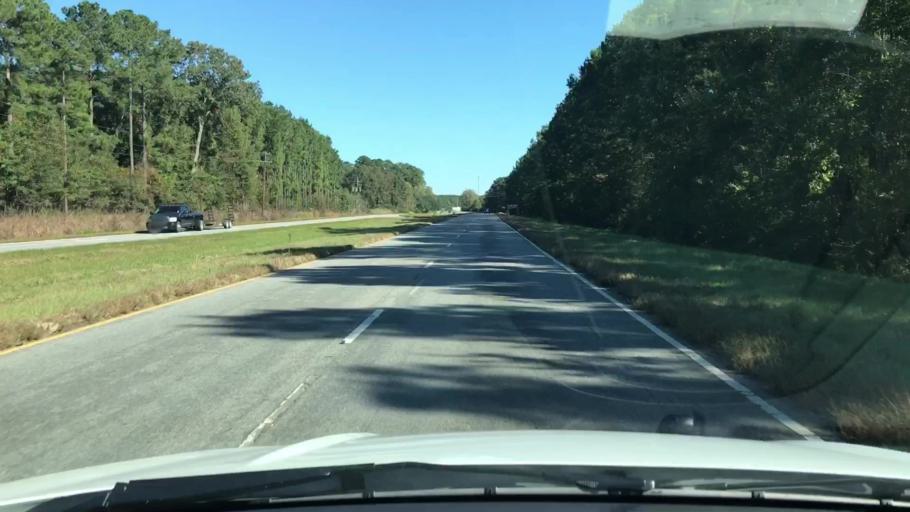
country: US
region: South Carolina
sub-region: Charleston County
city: Ravenel
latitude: 32.7600
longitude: -80.4009
